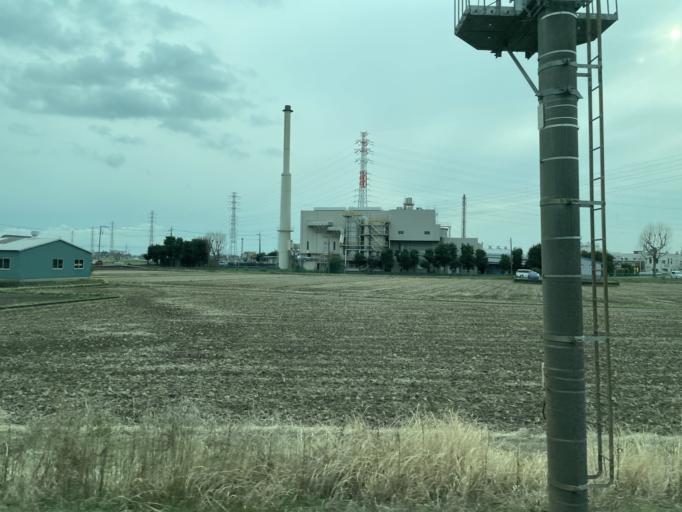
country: JP
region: Saitama
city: Kukichuo
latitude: 36.0486
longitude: 139.6892
